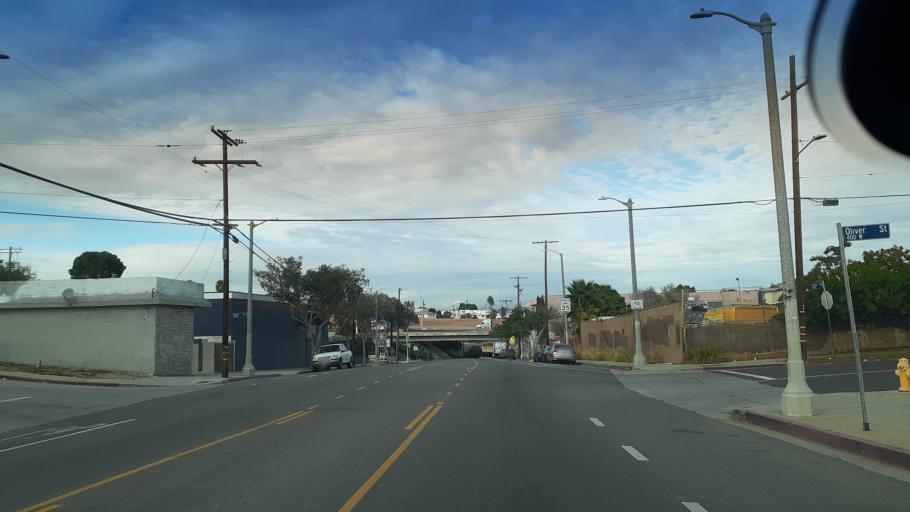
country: US
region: California
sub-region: Los Angeles County
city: San Pedro
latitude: 33.7467
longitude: -118.2879
